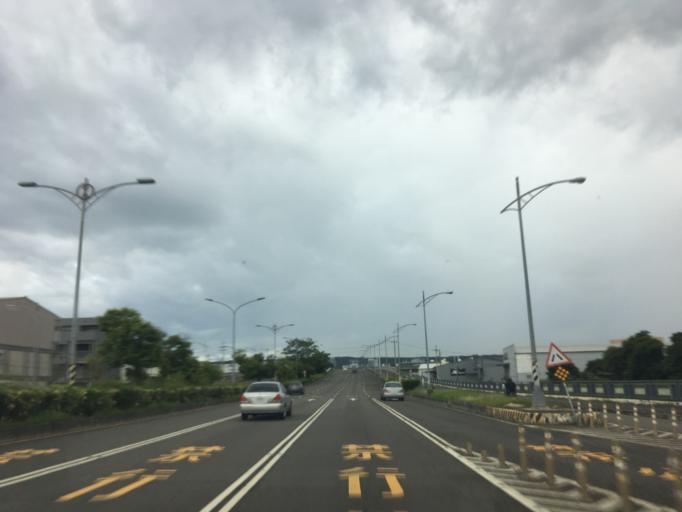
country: TW
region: Taiwan
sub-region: Taichung City
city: Taichung
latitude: 24.2027
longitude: 120.6405
